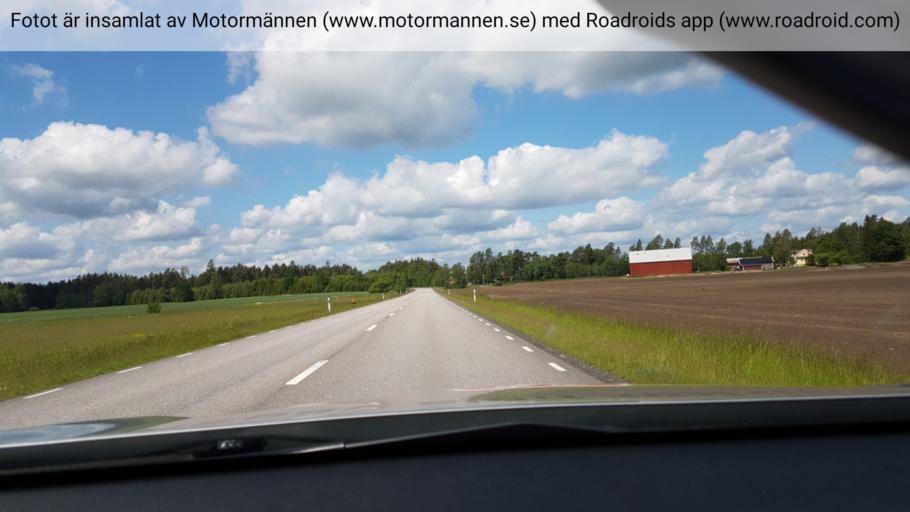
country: SE
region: Vaestra Goetaland
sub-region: Grastorps Kommun
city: Graestorp
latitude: 58.3271
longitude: 12.7212
